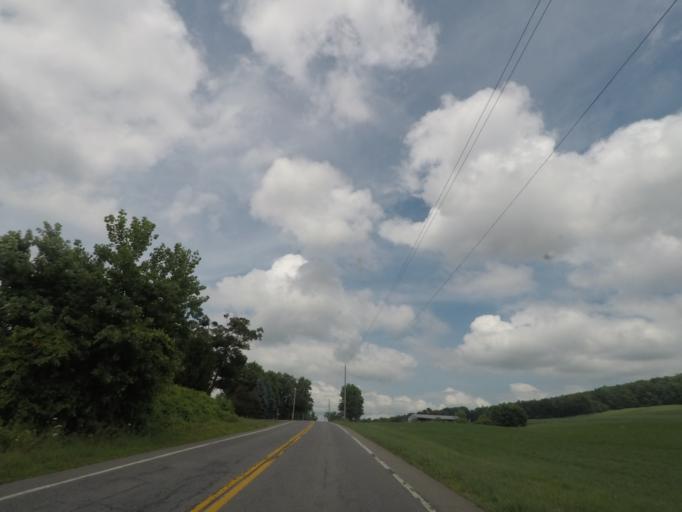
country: US
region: New York
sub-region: Saratoga County
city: Stillwater
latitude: 43.0384
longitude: -73.6819
